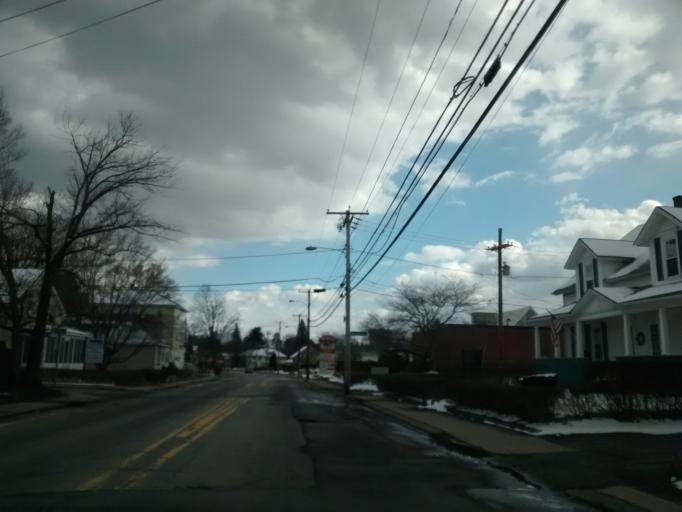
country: US
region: Massachusetts
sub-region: Worcester County
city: Uxbridge
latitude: 42.0833
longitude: -71.6390
